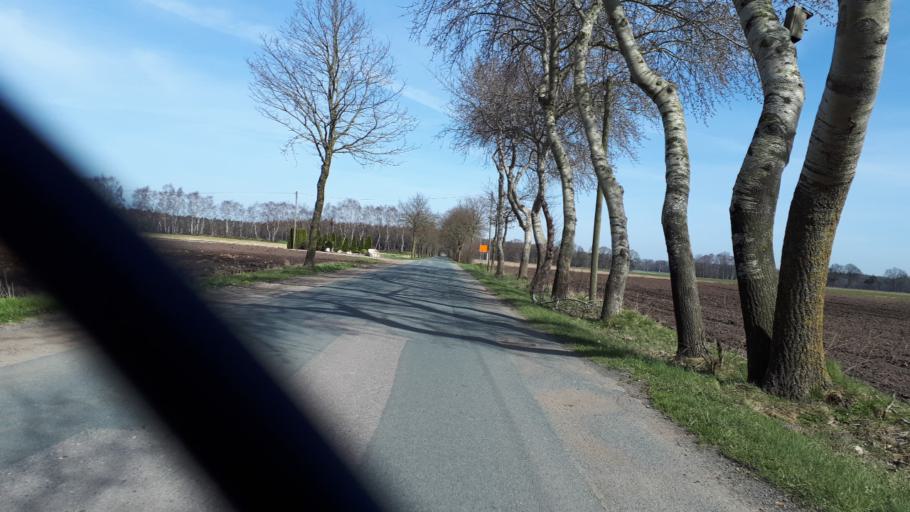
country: DE
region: Lower Saxony
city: Cloppenburg
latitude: 52.8790
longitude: 8.0005
